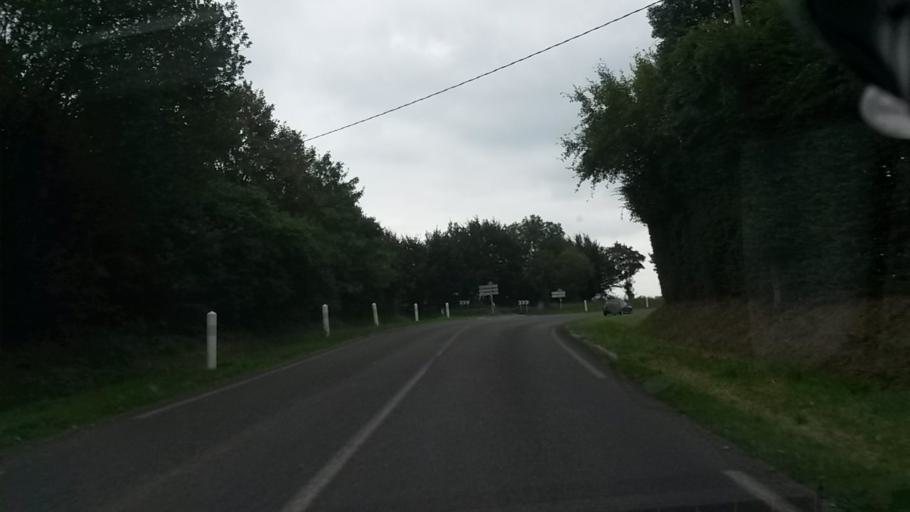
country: FR
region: Haute-Normandie
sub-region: Departement de la Seine-Maritime
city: Gaillefontaine
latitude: 49.6390
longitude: 1.6127
